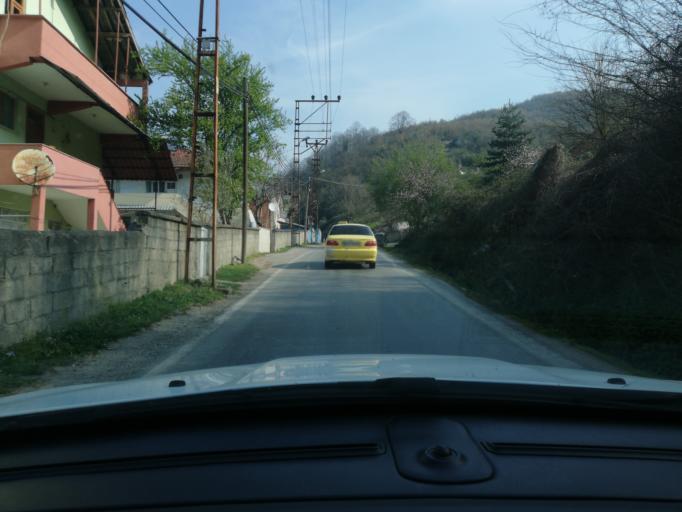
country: TR
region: Karabuk
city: Yenice
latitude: 41.2148
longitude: 32.3630
